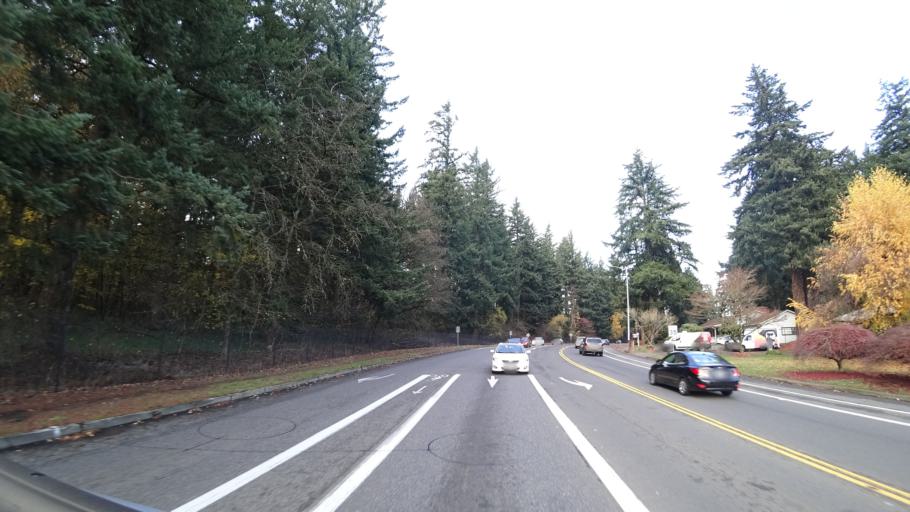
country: US
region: Oregon
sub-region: Multnomah County
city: Lents
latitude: 45.5267
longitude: -122.5107
